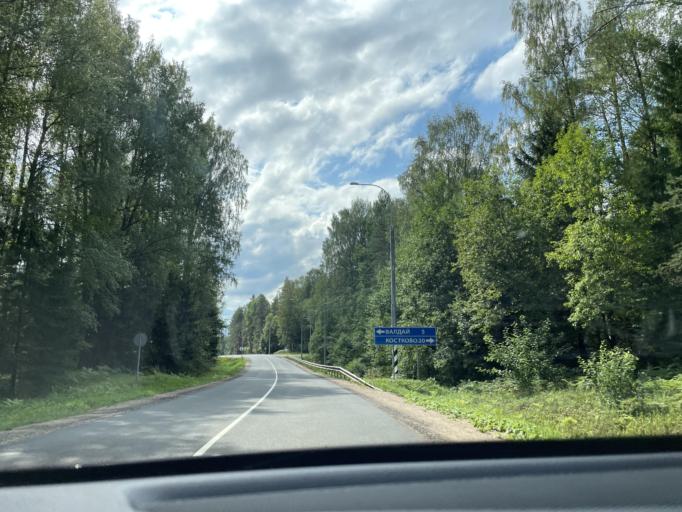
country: RU
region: Novgorod
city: Valday
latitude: 58.0287
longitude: 33.2006
